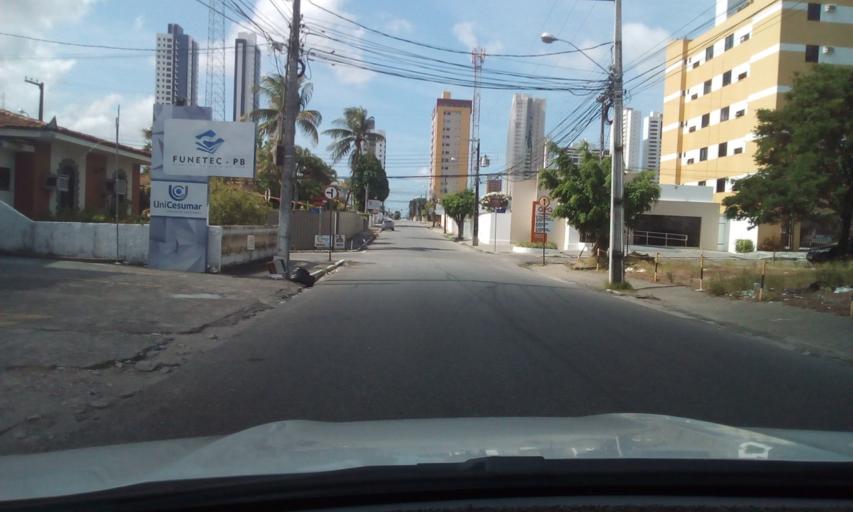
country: BR
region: Paraiba
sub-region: Joao Pessoa
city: Joao Pessoa
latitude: -7.1190
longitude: -34.8533
